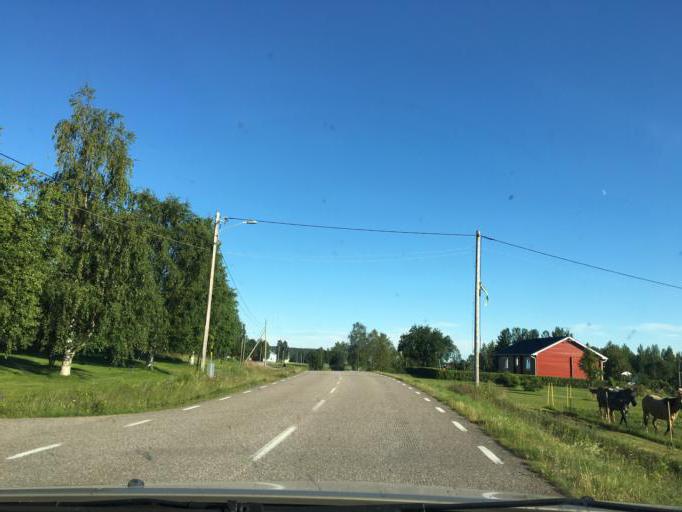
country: SE
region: Norrbotten
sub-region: Kalix Kommun
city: Rolfs
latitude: 65.9022
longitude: 22.9316
